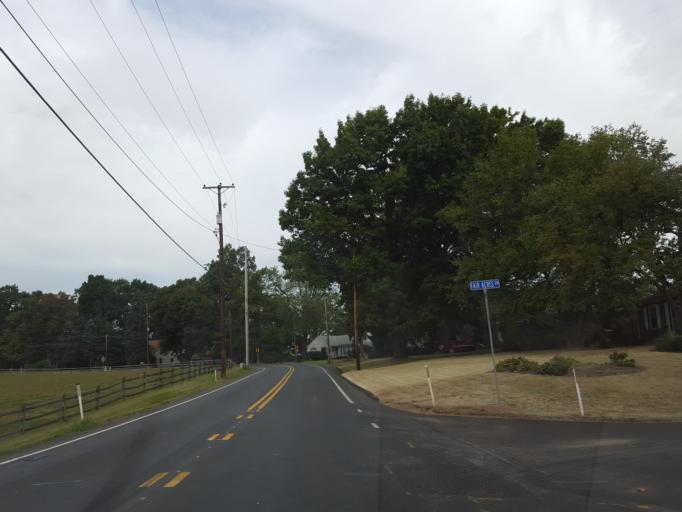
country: US
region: Pennsylvania
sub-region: York County
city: Grantley
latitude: 39.9118
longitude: -76.7197
